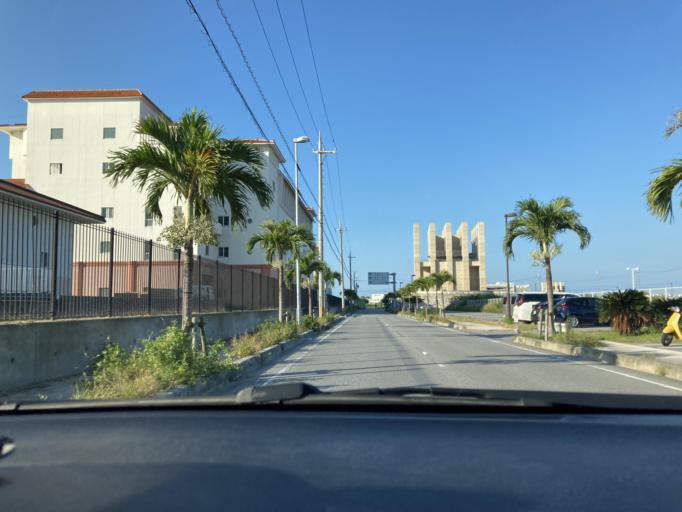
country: JP
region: Okinawa
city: Naha-shi
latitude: 26.2191
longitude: 127.6647
